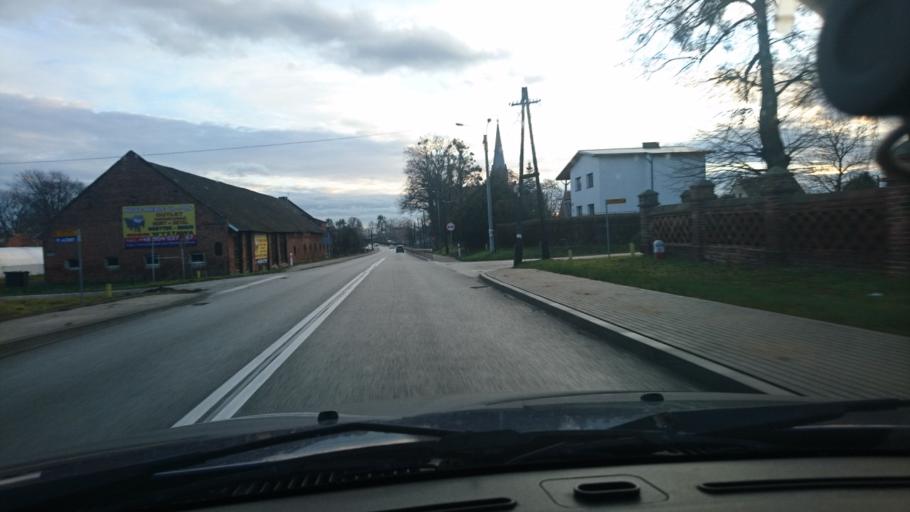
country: PL
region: Opole Voivodeship
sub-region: Powiat kluczborski
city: Kluczbork
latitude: 51.0300
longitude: 18.1923
